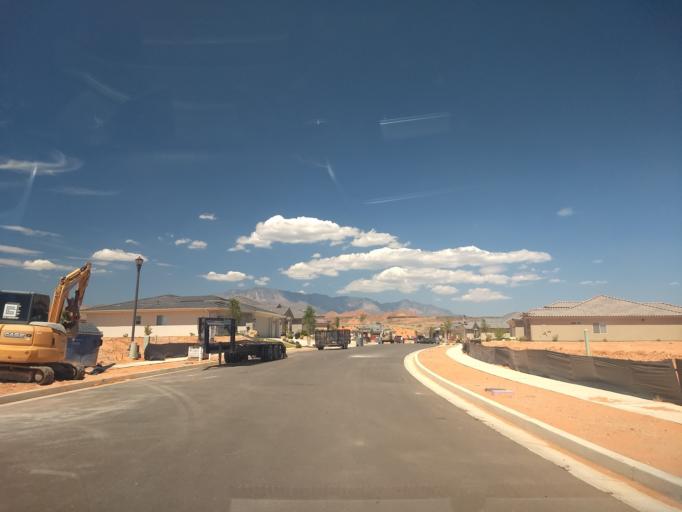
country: US
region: Utah
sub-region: Washington County
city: Washington
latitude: 37.1395
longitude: -113.4780
